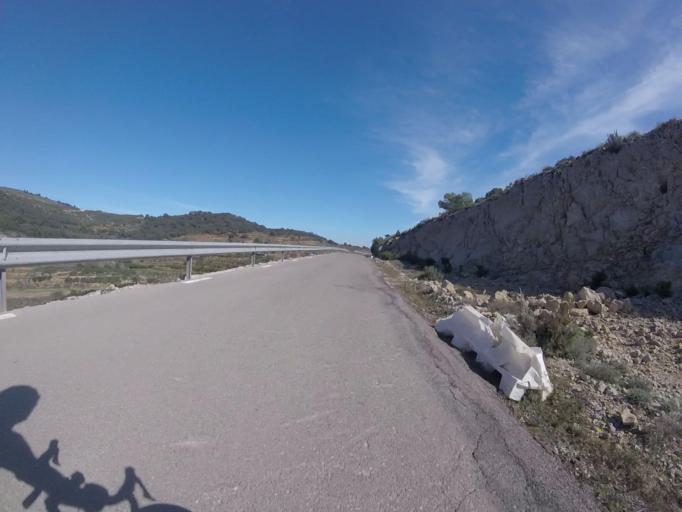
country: ES
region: Valencia
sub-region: Provincia de Castello
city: Sarratella
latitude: 40.3001
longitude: 0.0287
